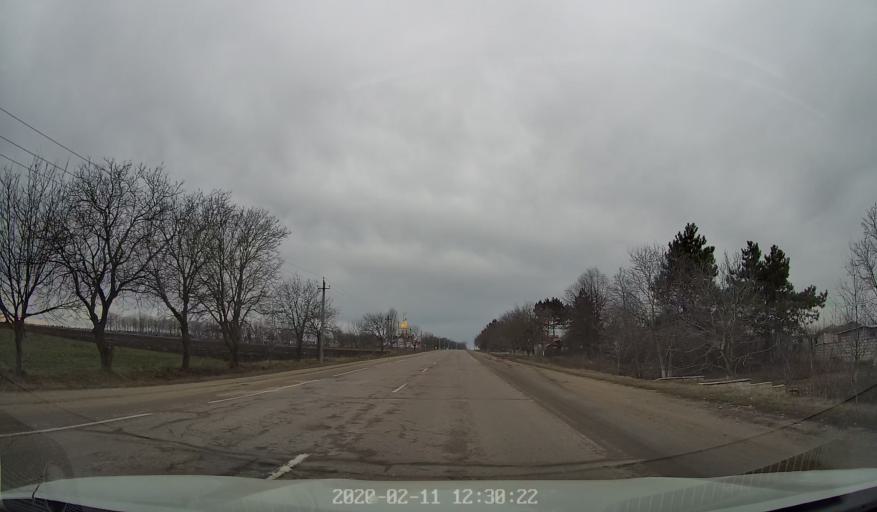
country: MD
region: Raionul Edinet
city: Edinet
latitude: 48.1628
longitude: 27.2838
